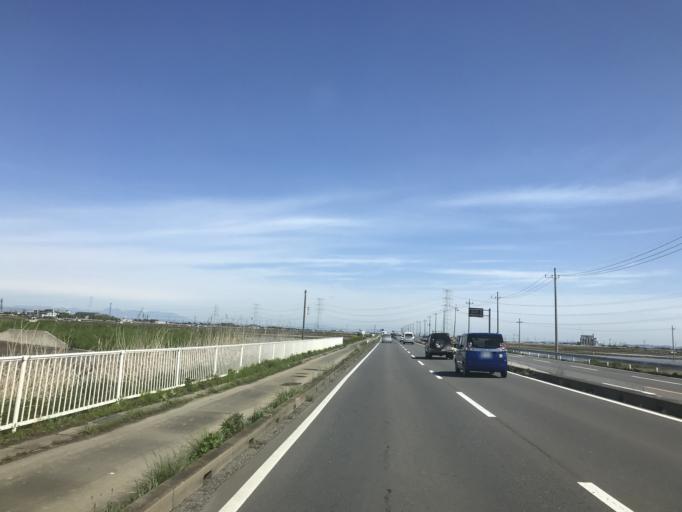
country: JP
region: Ibaraki
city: Ishige
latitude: 36.1148
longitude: 139.9833
